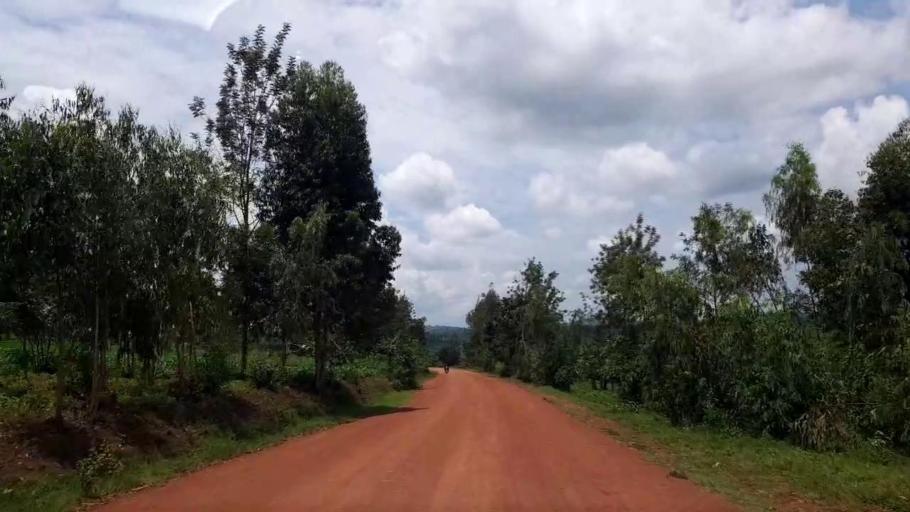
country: RW
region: Northern Province
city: Byumba
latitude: -1.5716
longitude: 30.3020
